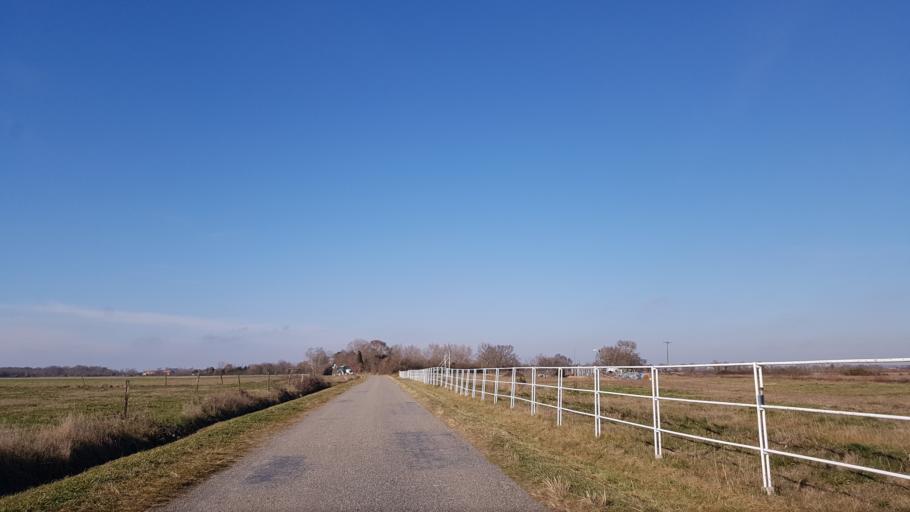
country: FR
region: Midi-Pyrenees
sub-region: Departement de l'Ariege
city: La Tour-du-Crieu
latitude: 43.1568
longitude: 1.6850
